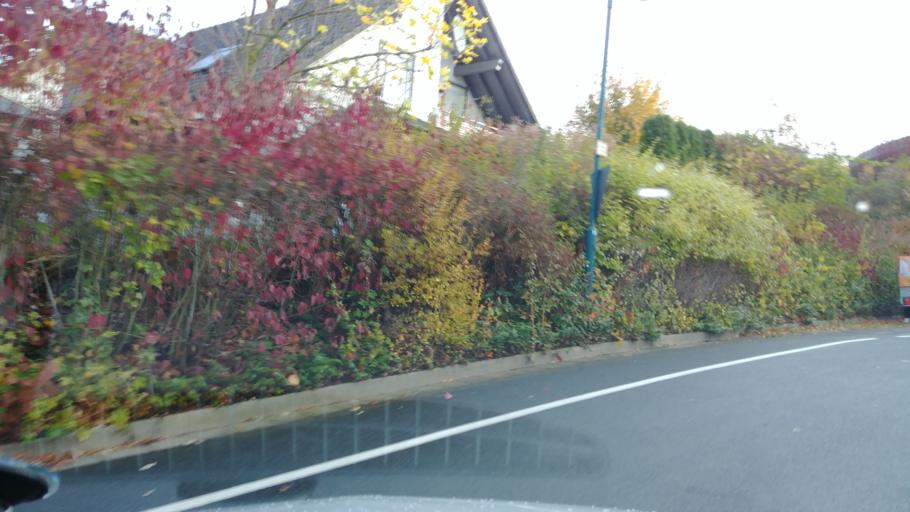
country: DE
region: Hesse
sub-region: Regierungsbezirk Darmstadt
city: Schlangenbad
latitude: 50.1264
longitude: 8.1234
